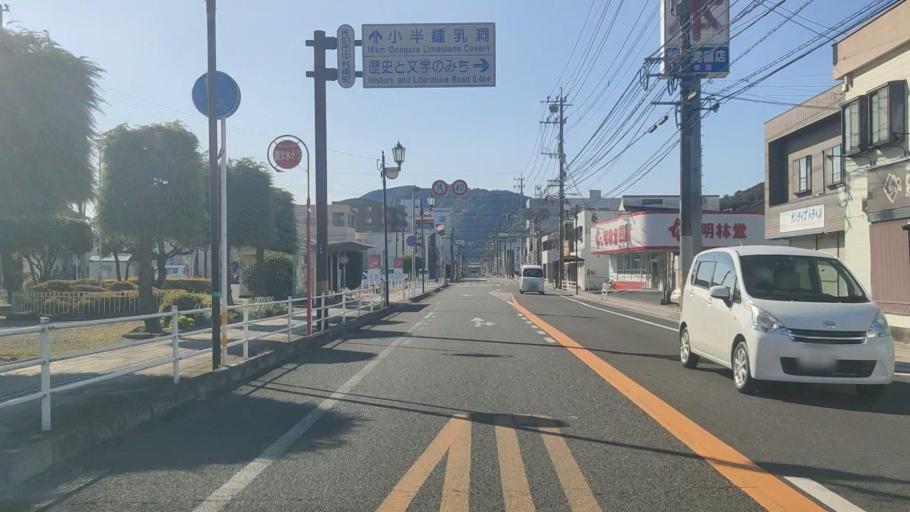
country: JP
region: Oita
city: Saiki
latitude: 32.9600
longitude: 131.8980
